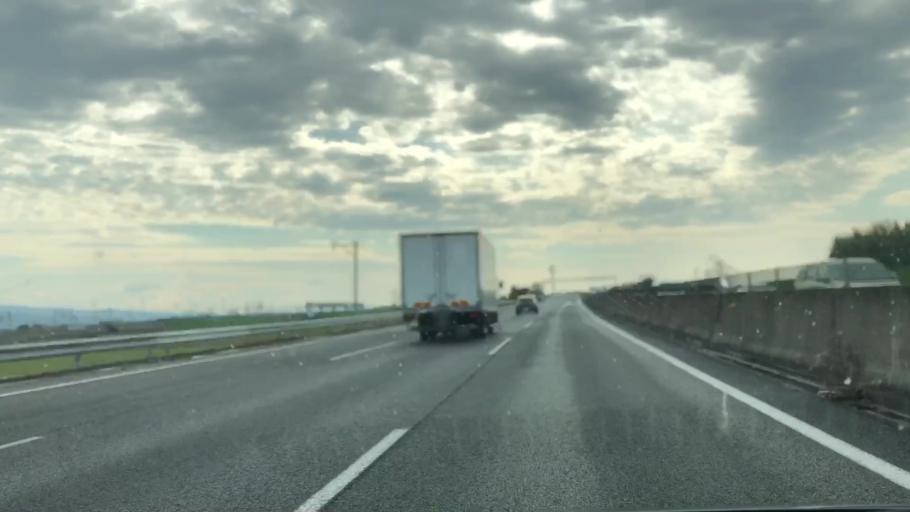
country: JP
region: Saga Prefecture
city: Tosu
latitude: 33.3601
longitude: 130.5402
